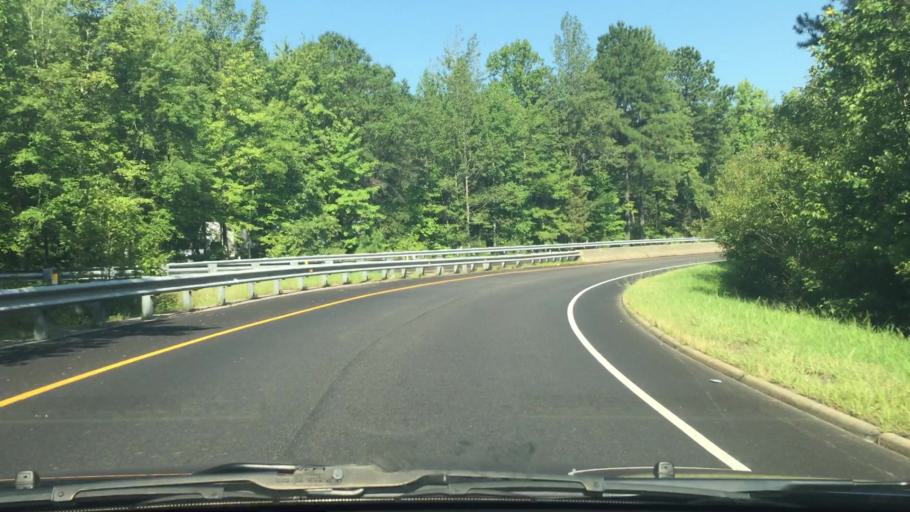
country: US
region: Virginia
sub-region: City of Petersburg
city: Petersburg
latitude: 37.0807
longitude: -77.3604
